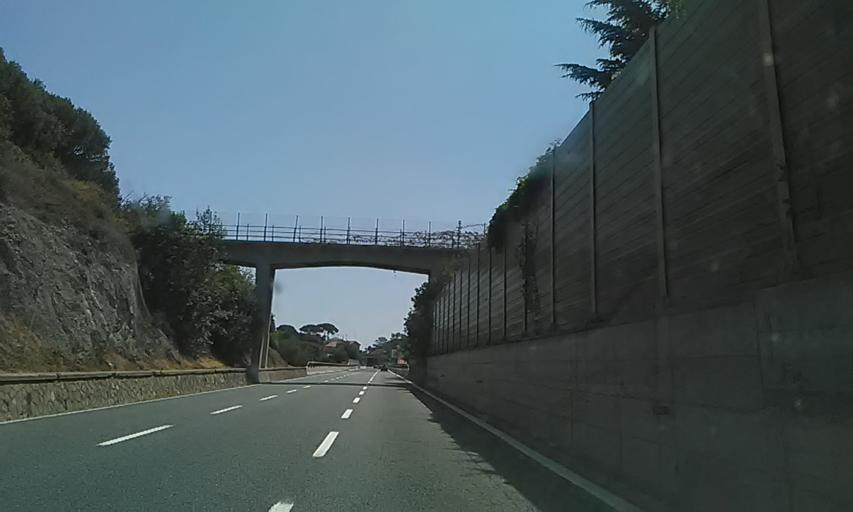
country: IT
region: Liguria
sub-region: Provincia di Savona
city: Celle Ligure
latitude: 44.3478
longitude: 8.5491
